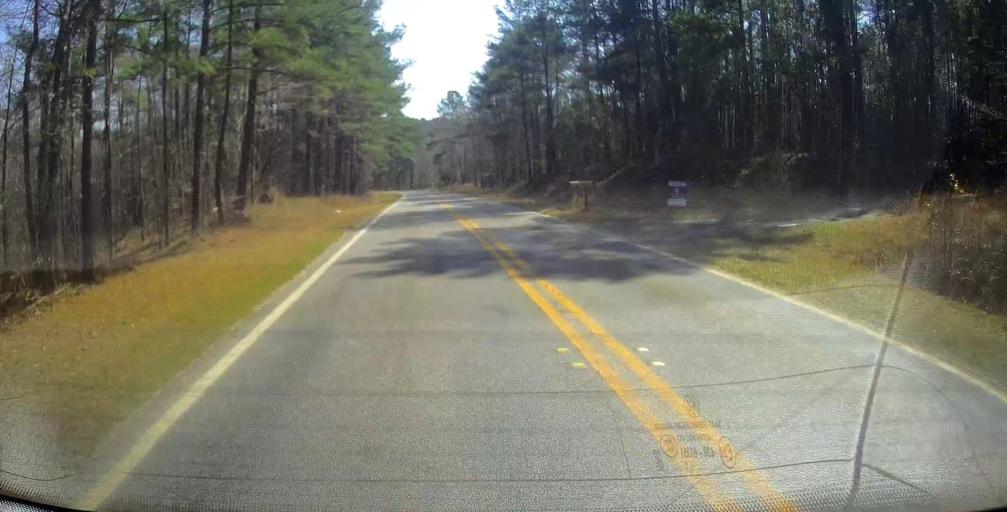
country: US
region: Georgia
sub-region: Jones County
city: Gray
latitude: 32.9295
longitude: -83.5345
